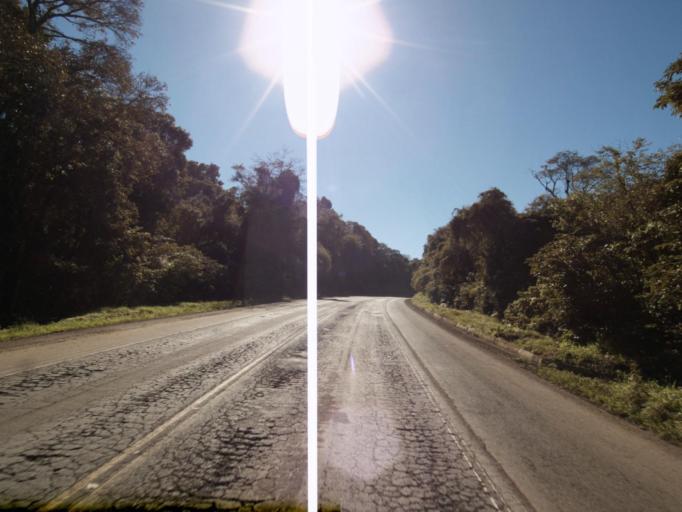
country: BR
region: Rio Grande do Sul
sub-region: Frederico Westphalen
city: Frederico Westphalen
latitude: -26.9214
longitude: -53.1987
